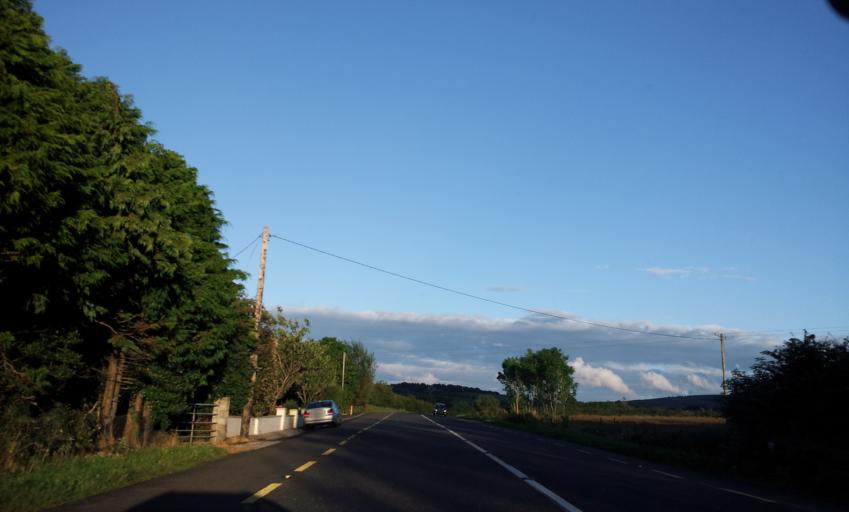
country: IE
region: Munster
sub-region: County Limerick
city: Abbeyfeale
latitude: 52.3861
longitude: -9.2338
